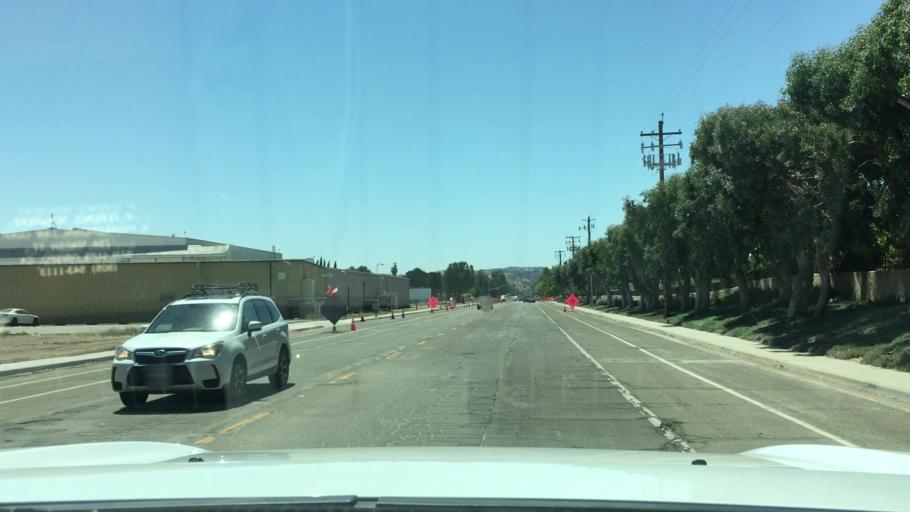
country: US
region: California
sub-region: San Luis Obispo County
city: Paso Robles
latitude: 35.6157
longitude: -120.6543
